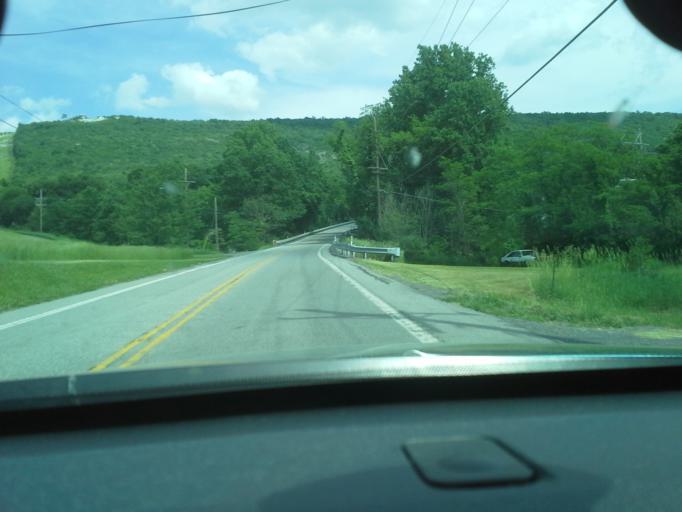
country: US
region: Pennsylvania
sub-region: Fulton County
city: McConnellsburg
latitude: 39.9169
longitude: -77.9716
